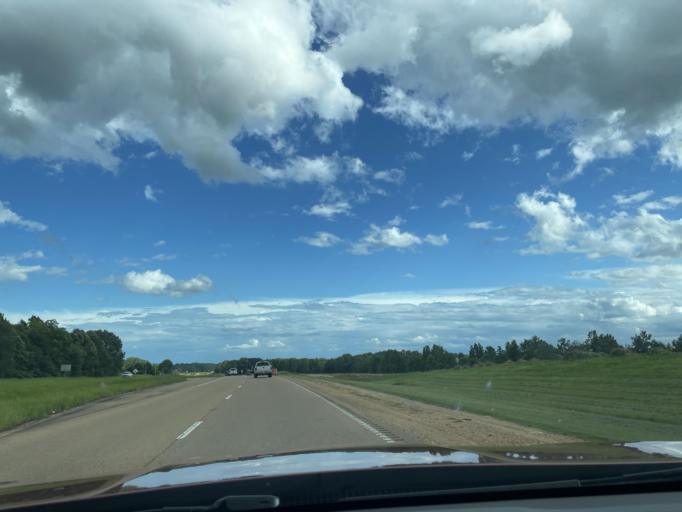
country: US
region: Mississippi
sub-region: Madison County
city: Flora
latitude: 32.5372
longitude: -90.3191
